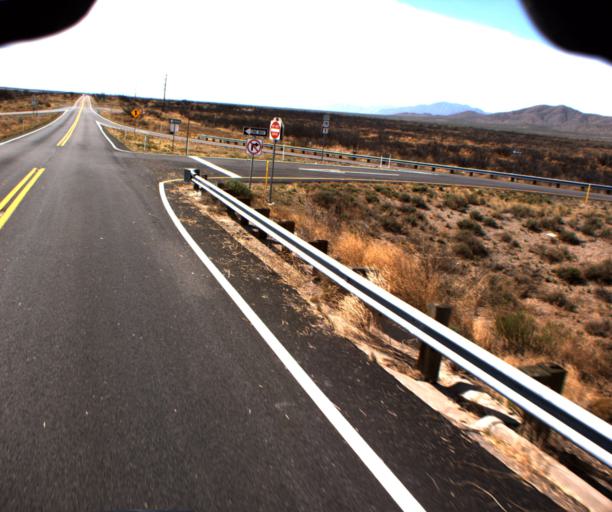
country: US
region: Arizona
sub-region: Cochise County
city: Willcox
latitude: 32.1750
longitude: -109.9487
